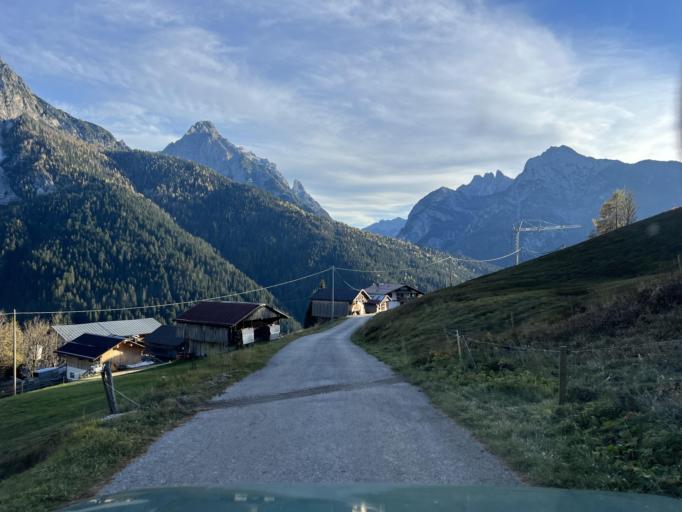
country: IT
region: Veneto
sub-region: Provincia di Belluno
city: San Pietro di Cadore
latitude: 46.5798
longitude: 12.5960
